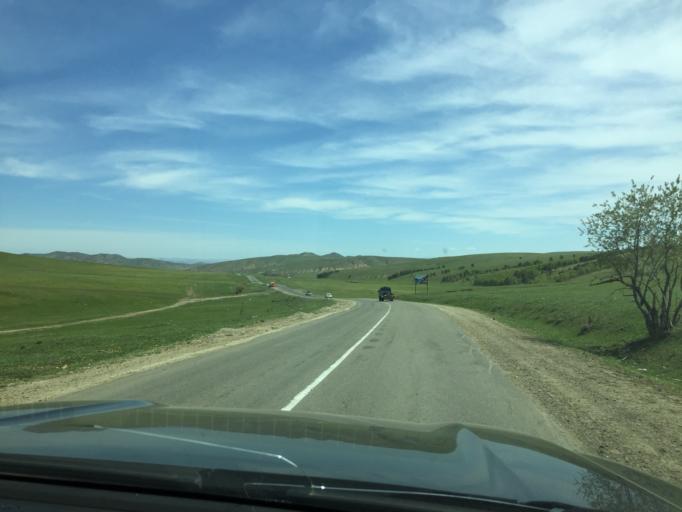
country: MN
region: Central Aimak
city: Javhlant
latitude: 48.6522
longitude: 106.1071
